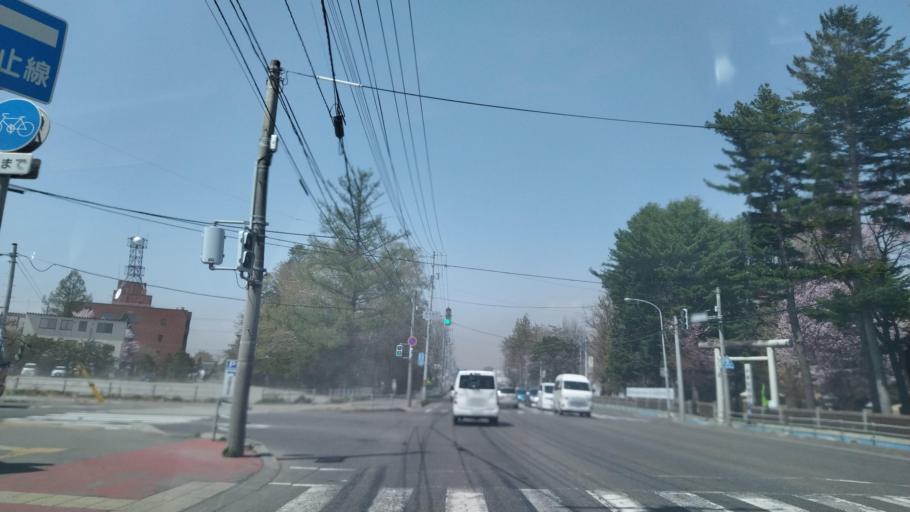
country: JP
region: Hokkaido
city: Obihiro
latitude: 42.9300
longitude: 143.2111
